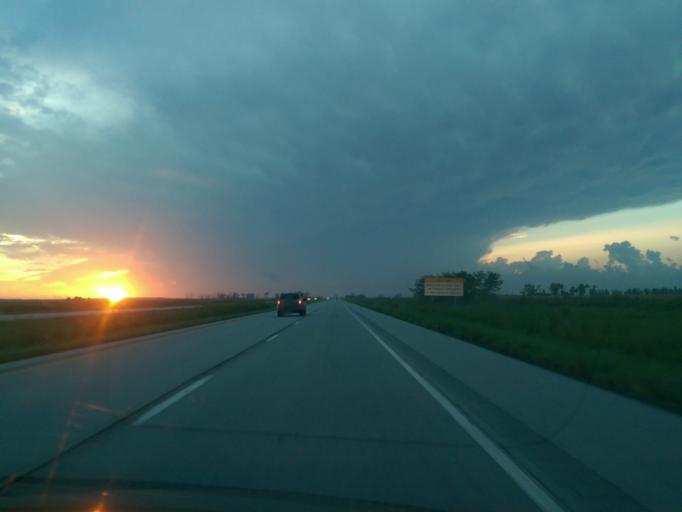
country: US
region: Iowa
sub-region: Fremont County
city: Hamburg
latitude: 40.6103
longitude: -95.6877
